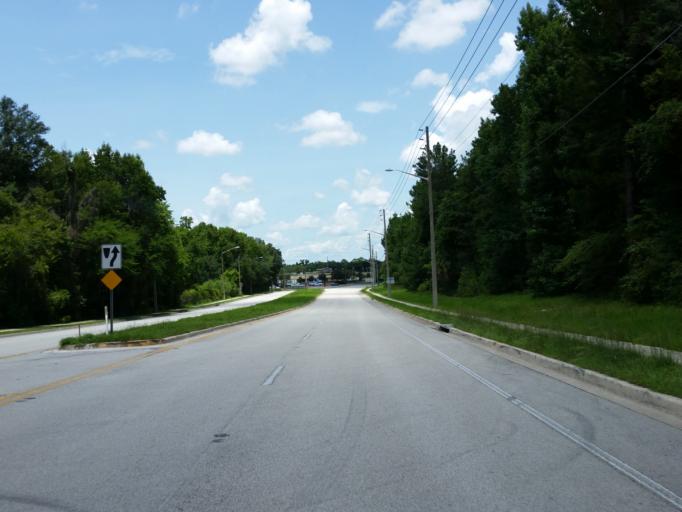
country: US
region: Florida
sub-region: Alachua County
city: Gainesville
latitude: 29.6009
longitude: -82.3685
